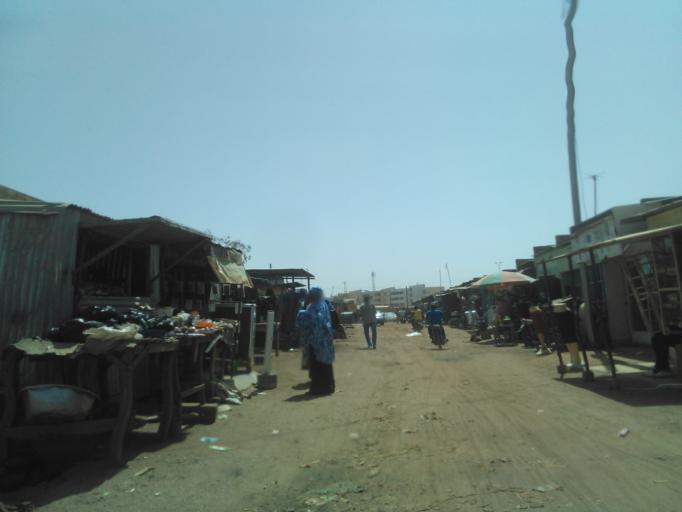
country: BF
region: Centre
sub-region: Kadiogo Province
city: Ouagadougou
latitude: 12.3897
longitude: -1.5646
